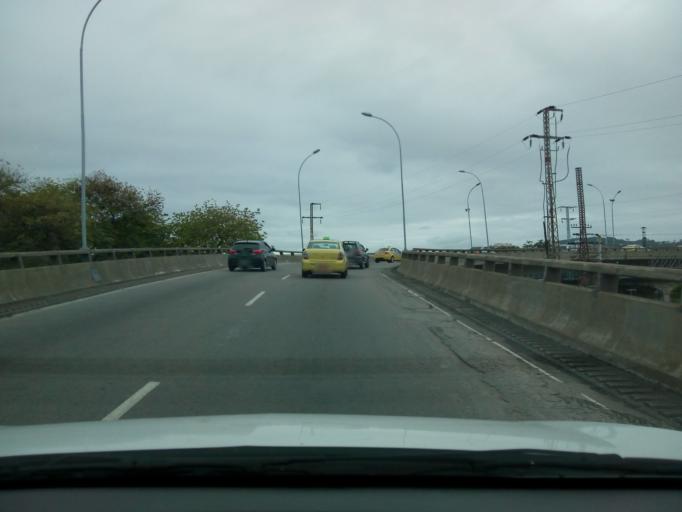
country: BR
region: Rio de Janeiro
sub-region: Rio De Janeiro
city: Rio de Janeiro
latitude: -22.9094
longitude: -43.2248
